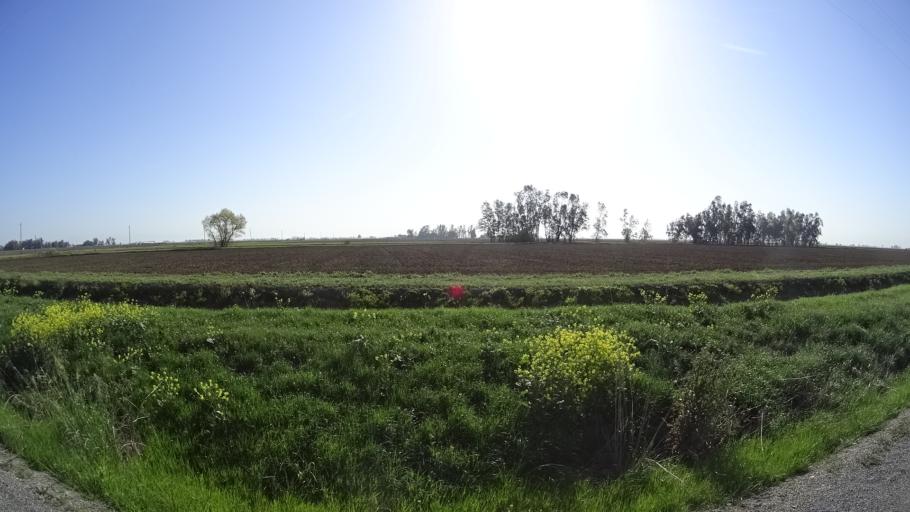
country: US
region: California
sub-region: Glenn County
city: Willows
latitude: 39.5738
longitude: -122.1080
